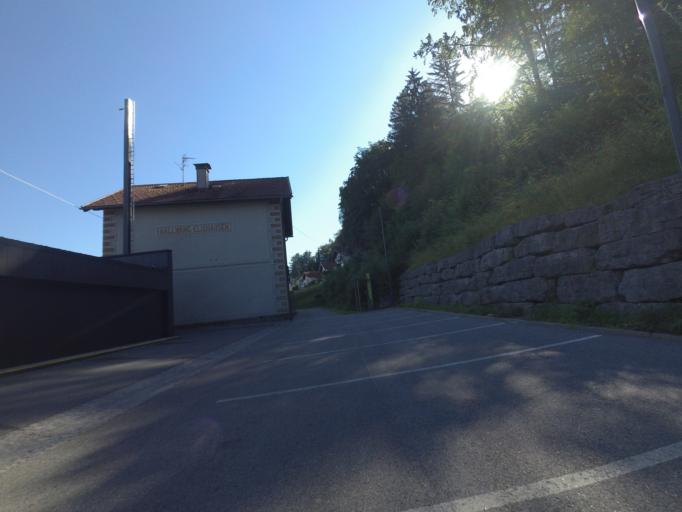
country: AT
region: Salzburg
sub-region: Politischer Bezirk Salzburg-Umgebung
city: Hallwang
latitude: 47.8576
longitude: 13.0917
